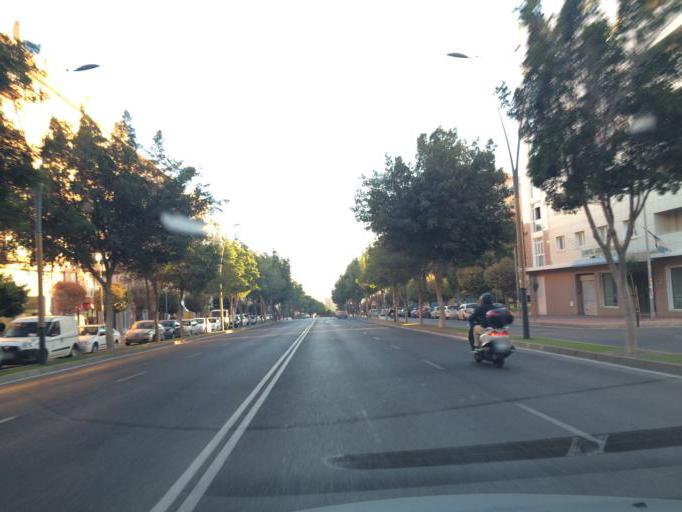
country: ES
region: Andalusia
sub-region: Provincia de Almeria
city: Almeria
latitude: 36.8503
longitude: -2.4465
